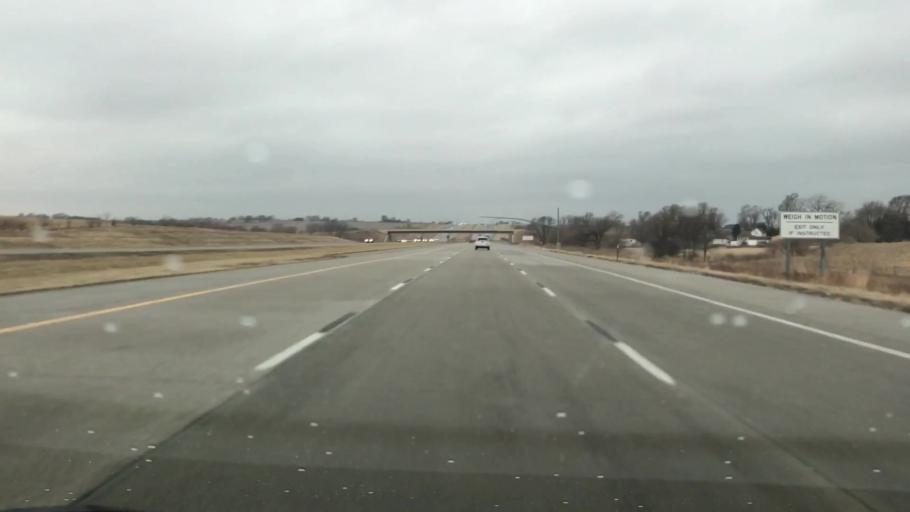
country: US
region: Nebraska
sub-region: Lancaster County
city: Waverly
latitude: 40.9320
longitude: -96.4410
